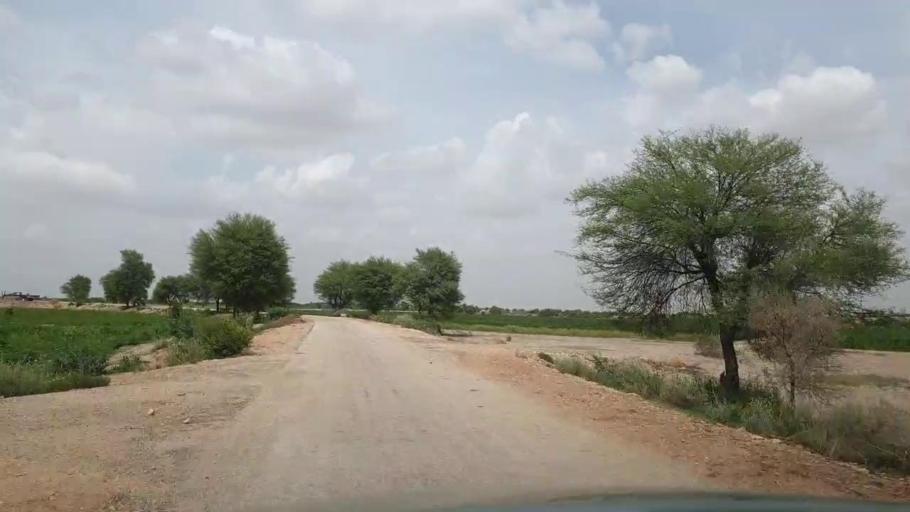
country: PK
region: Sindh
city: Kot Diji
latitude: 27.2274
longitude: 69.0886
